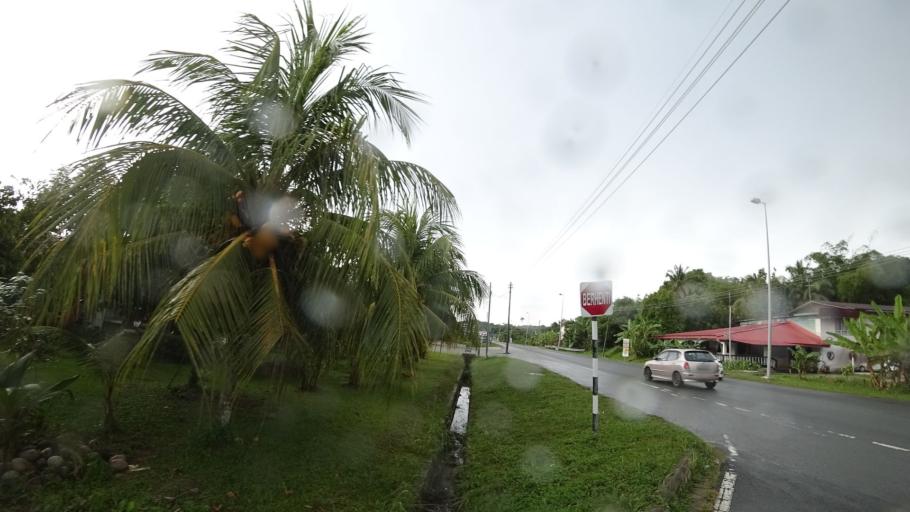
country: BN
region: Brunei and Muara
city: Bandar Seri Begawan
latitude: 4.8347
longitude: 114.9165
